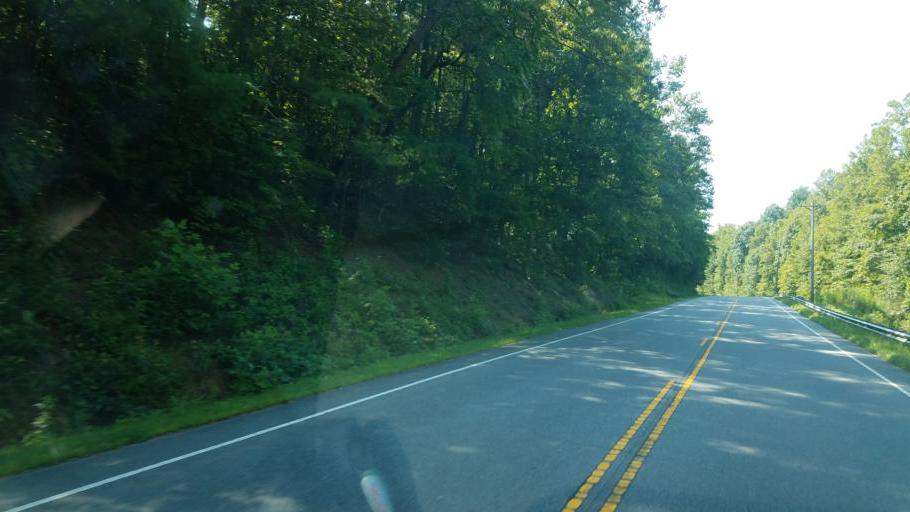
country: US
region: North Carolina
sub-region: Burke County
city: Glen Alpine
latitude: 35.8172
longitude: -81.7907
